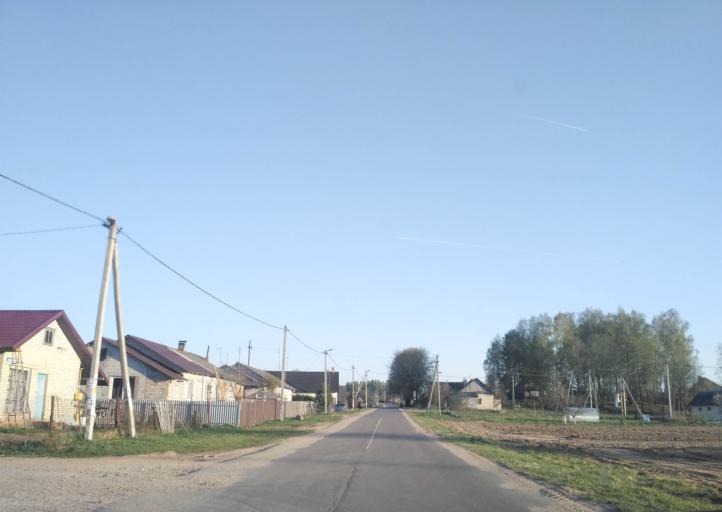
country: BY
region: Minsk
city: Pyatryshki
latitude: 54.1073
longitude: 27.1919
